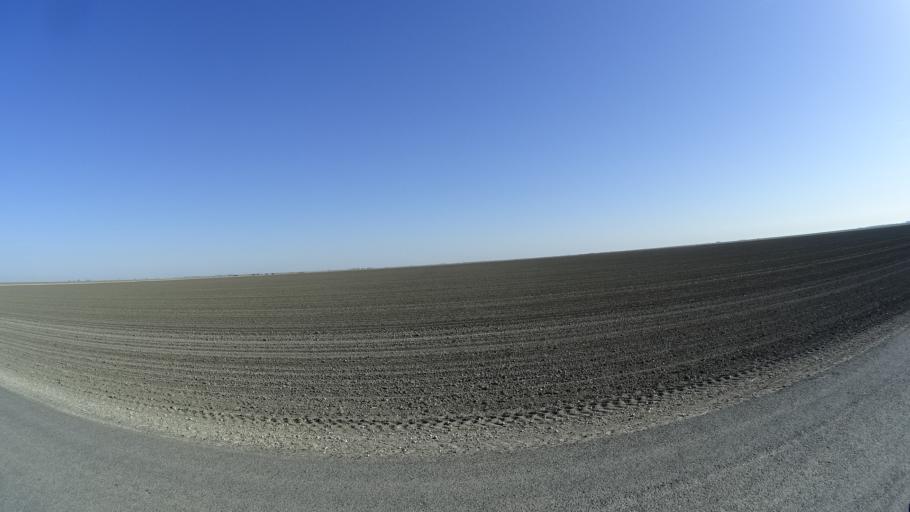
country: US
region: California
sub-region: Kings County
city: Corcoran
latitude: 36.0797
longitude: -119.7038
